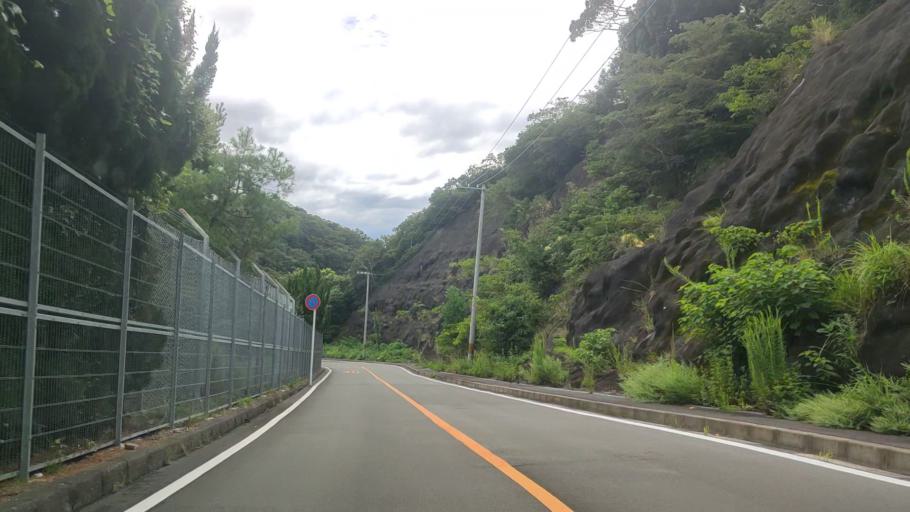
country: JP
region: Wakayama
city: Tanabe
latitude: 33.6636
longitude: 135.3681
